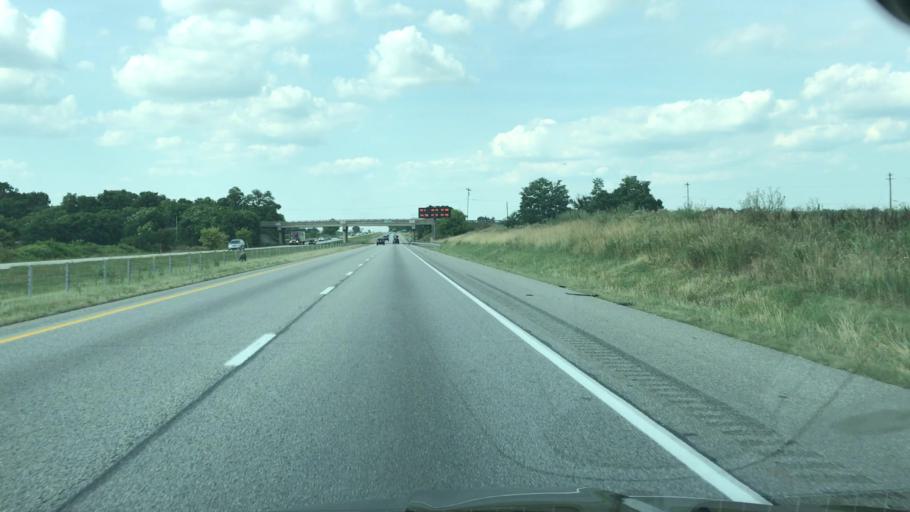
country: US
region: Pennsylvania
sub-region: Franklin County
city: Chambersburg
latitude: 39.8745
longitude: -77.6783
